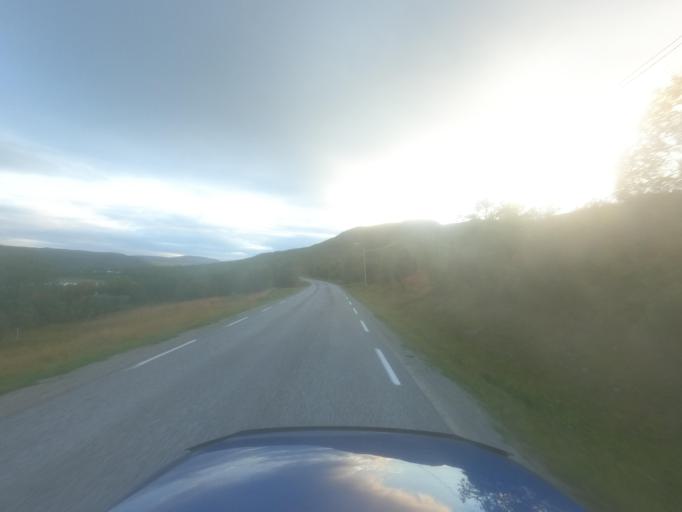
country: NO
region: Finnmark Fylke
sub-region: Porsanger
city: Lakselv
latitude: 70.3583
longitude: 25.0464
